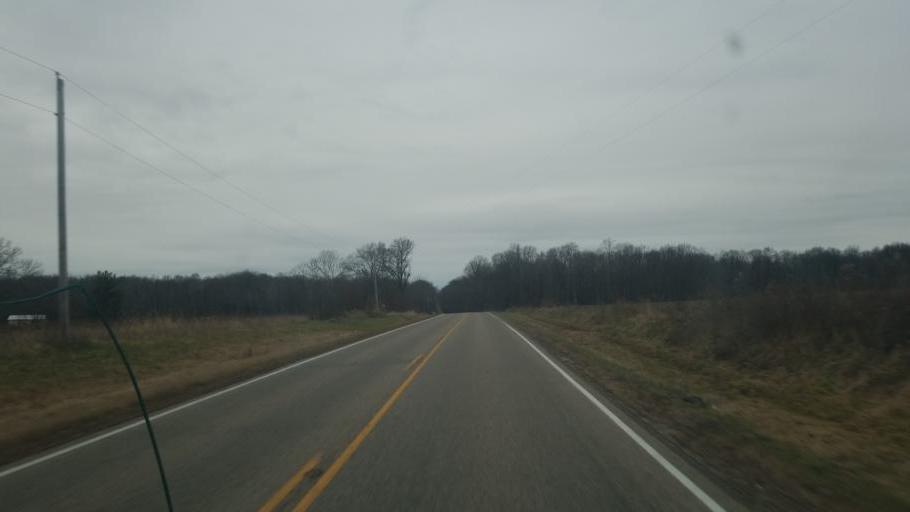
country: US
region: Indiana
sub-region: Clay County
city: Middlebury
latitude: 39.3626
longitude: -86.9577
